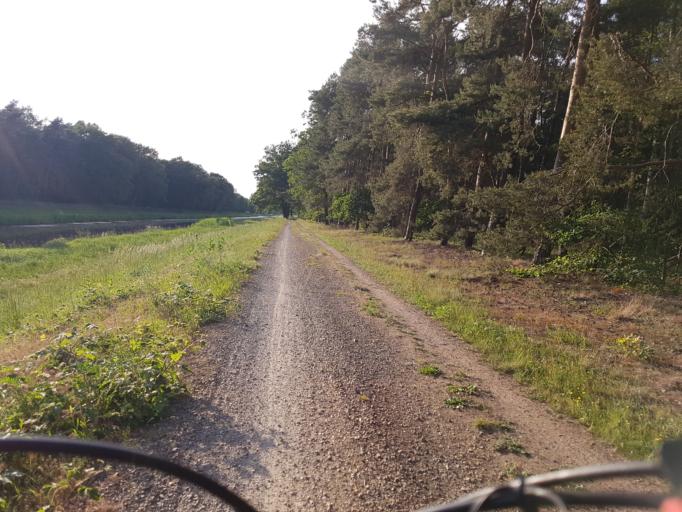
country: DE
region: Brandenburg
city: Bad Liebenwerda
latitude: 51.4871
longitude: 13.4333
